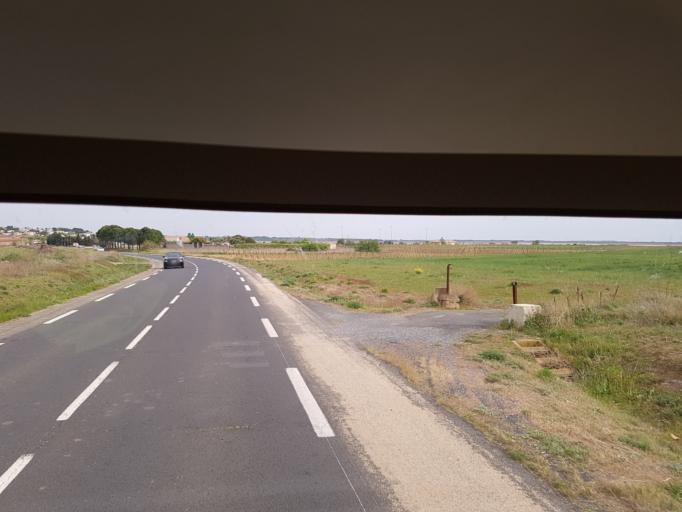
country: FR
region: Languedoc-Roussillon
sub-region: Departement de l'Herault
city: Vendres
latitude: 43.2718
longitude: 3.2115
